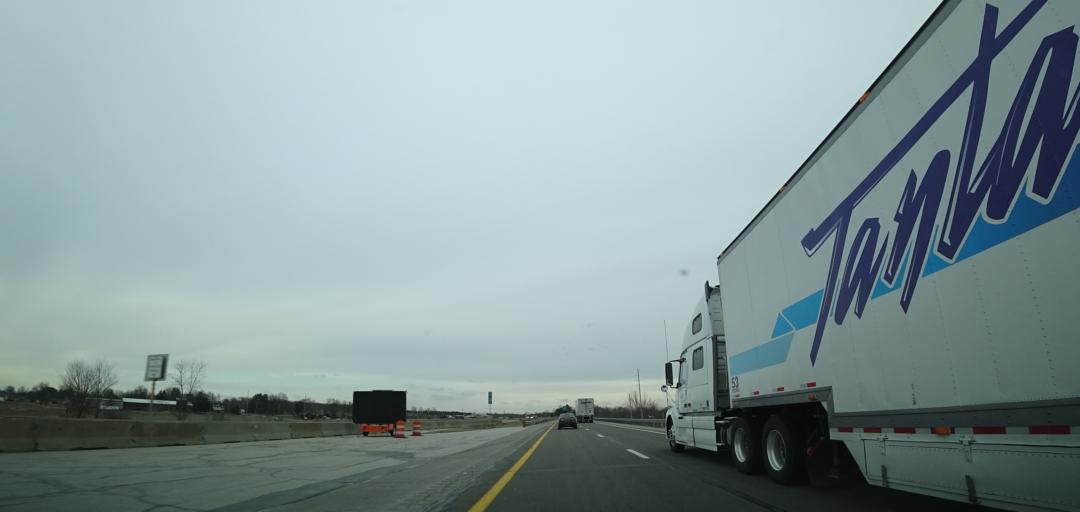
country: US
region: Ohio
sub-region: Mahoning County
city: Boardman
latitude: 40.9897
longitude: -80.6897
